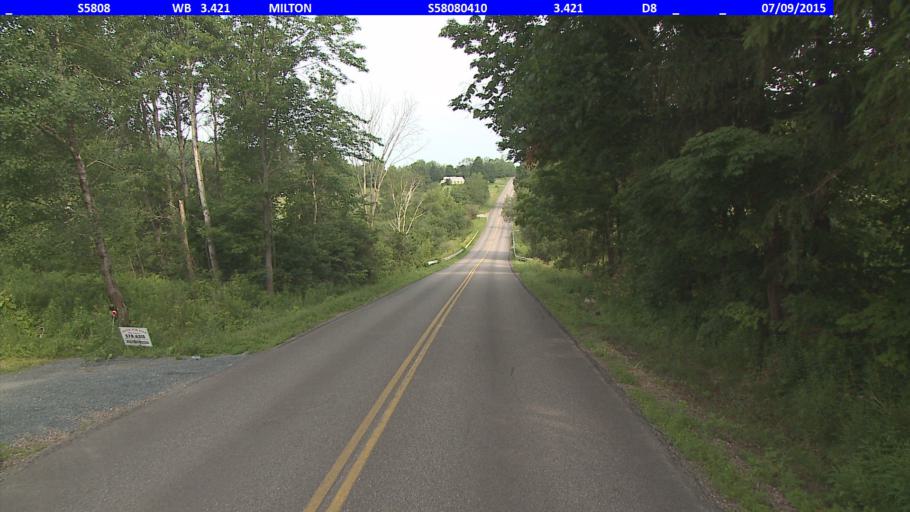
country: US
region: Vermont
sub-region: Chittenden County
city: Milton
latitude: 44.6381
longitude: -73.0531
